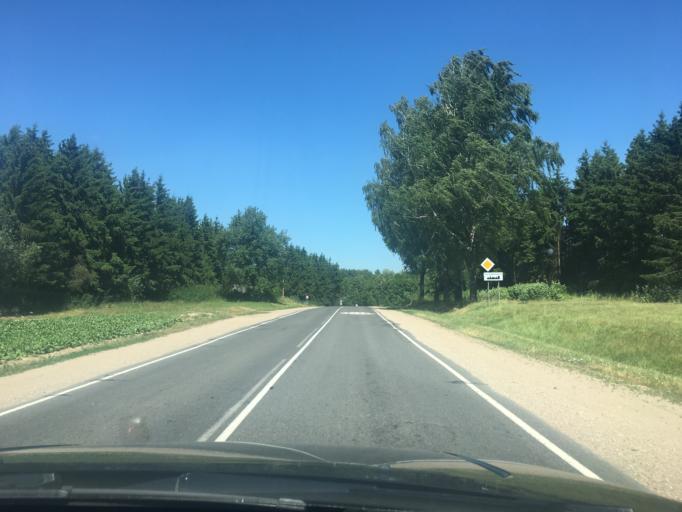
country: BY
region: Grodnenskaya
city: Hal'shany
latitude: 54.2122
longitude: 25.9648
